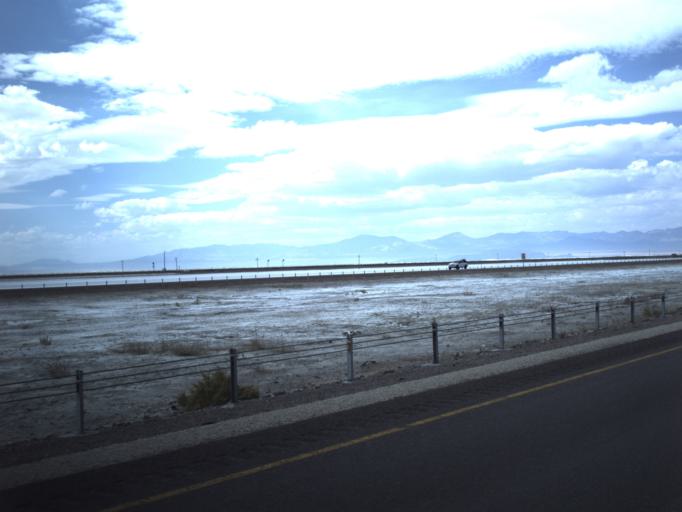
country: US
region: Utah
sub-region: Tooele County
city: Wendover
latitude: 40.7392
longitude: -113.8401
